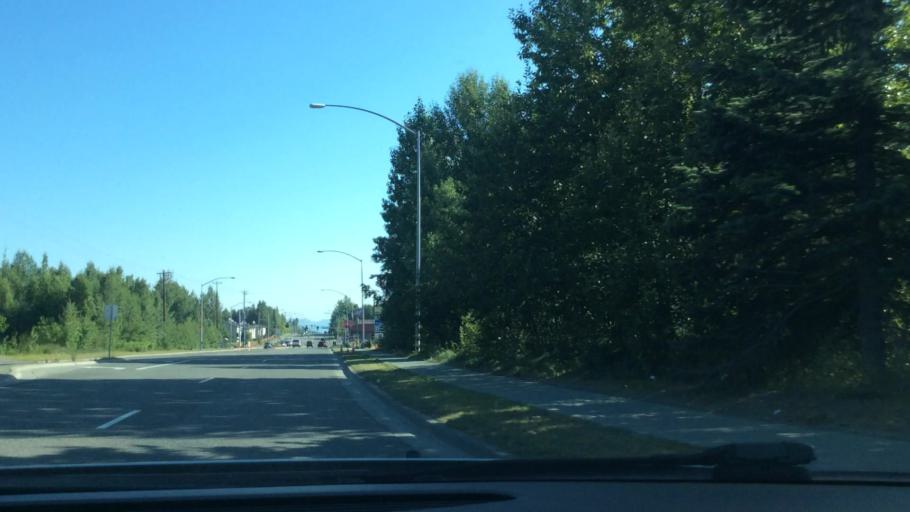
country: US
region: Alaska
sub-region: Anchorage Municipality
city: Anchorage
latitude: 61.1618
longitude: -149.8345
